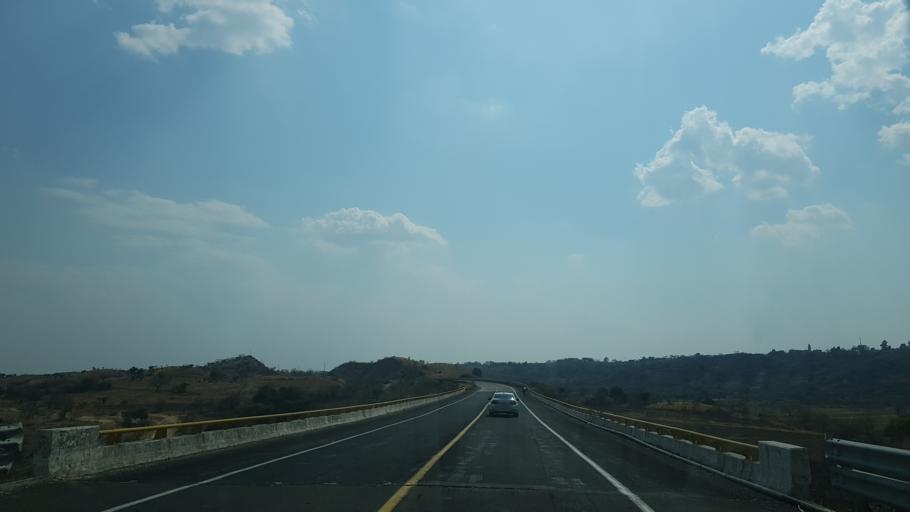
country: MX
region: Puebla
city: San Juan Amecac
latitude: 18.8118
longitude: -98.6997
